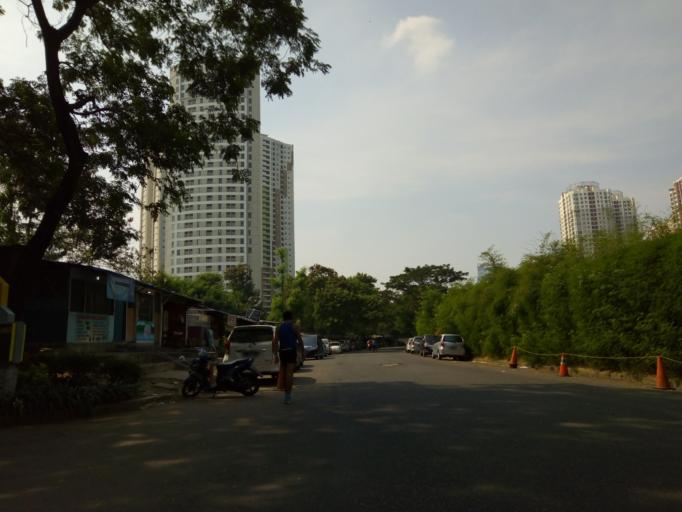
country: ID
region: Jakarta Raya
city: Jakarta
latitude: -6.2133
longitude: 106.8353
